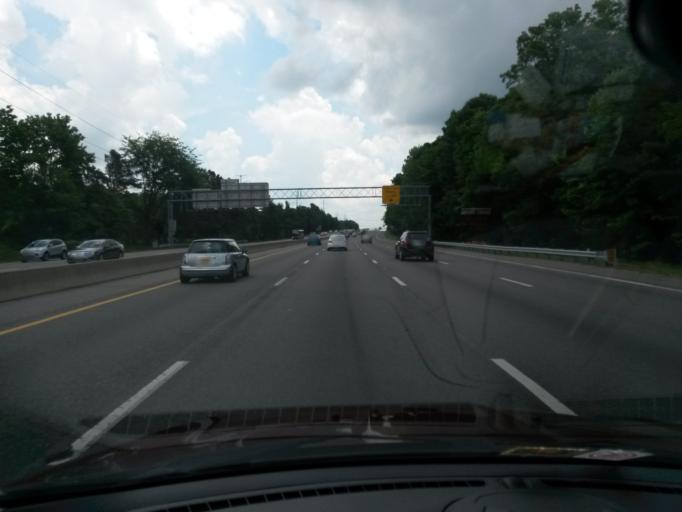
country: US
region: Virginia
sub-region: Chesterfield County
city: Bellwood
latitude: 37.4242
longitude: -77.4288
